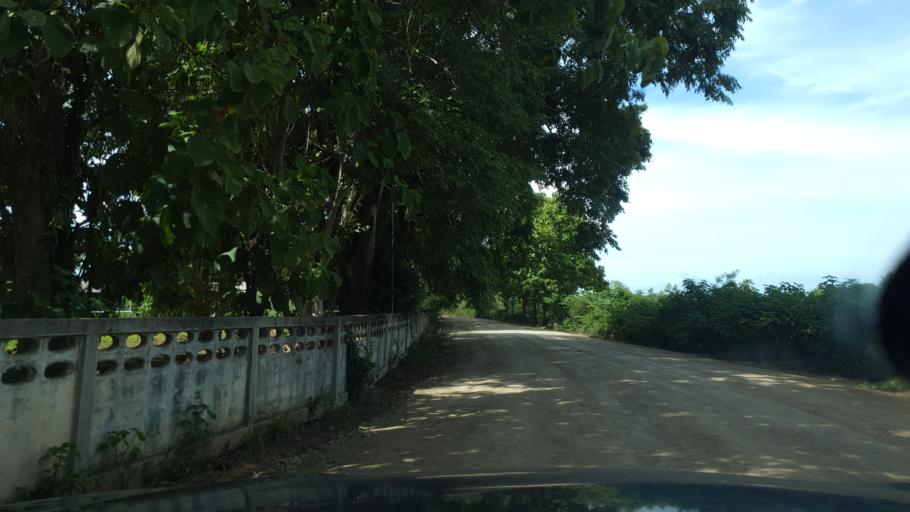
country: TH
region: Sukhothai
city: Sawankhalok
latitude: 17.2151
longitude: 99.7183
